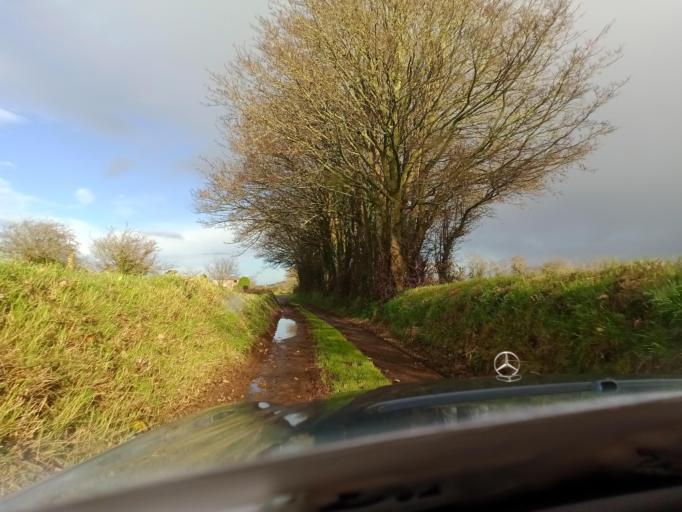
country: IE
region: Leinster
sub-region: Kilkenny
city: Mooncoin
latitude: 52.2969
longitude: -7.2716
